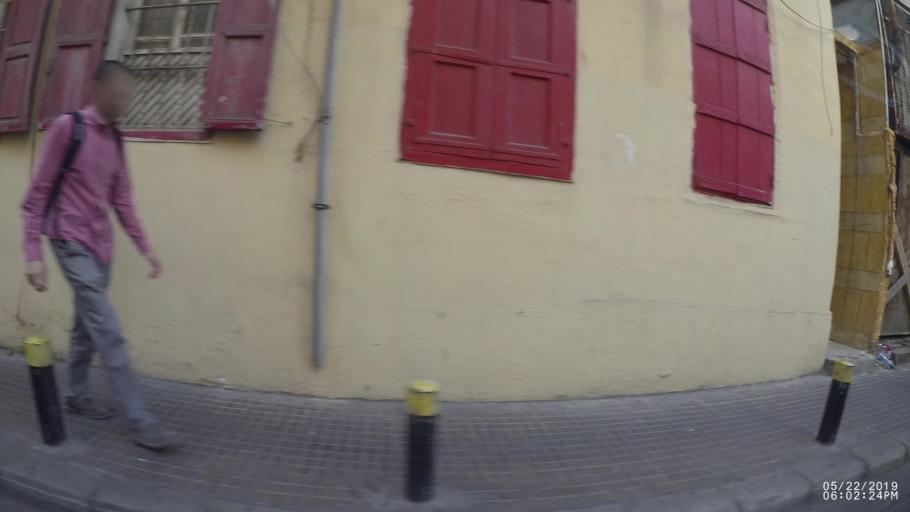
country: LB
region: Beyrouth
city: Ra's Bayrut
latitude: 33.8976
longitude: 35.4786
